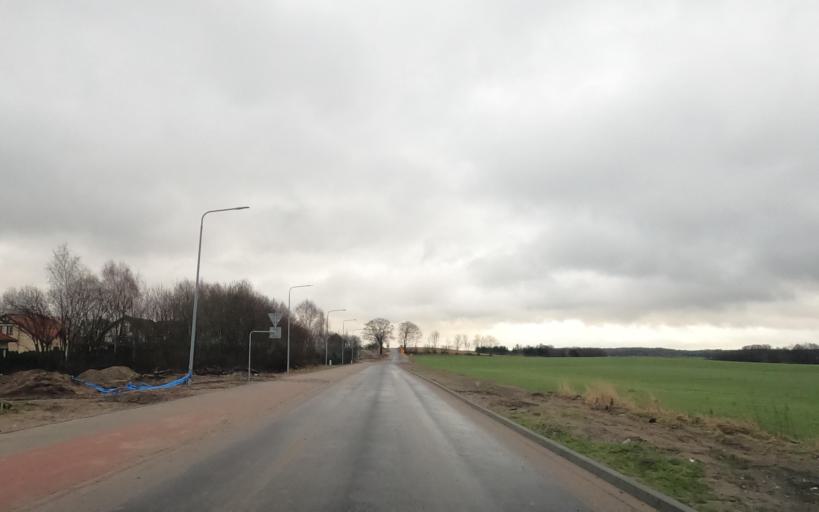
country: PL
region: West Pomeranian Voivodeship
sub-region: Powiat szczecinecki
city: Szczecinek
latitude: 53.7111
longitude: 16.7318
